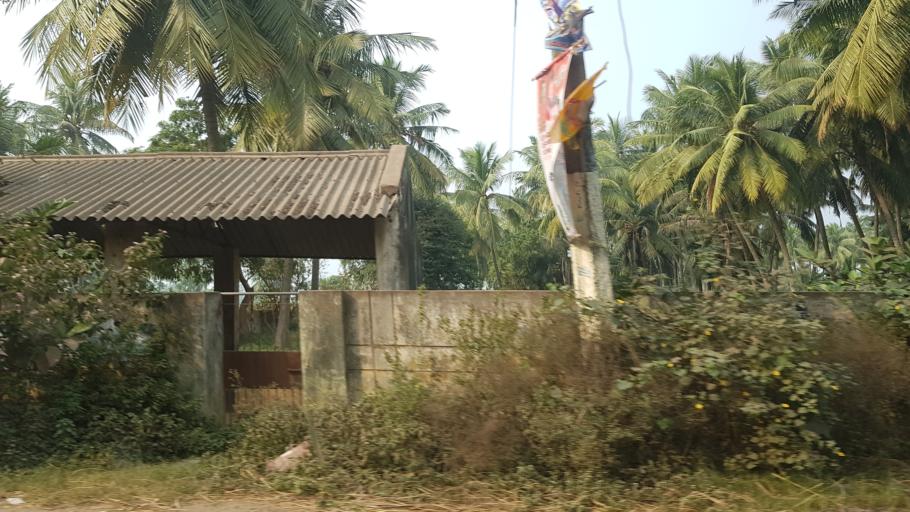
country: IN
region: Andhra Pradesh
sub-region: West Godavari
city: Akividu
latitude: 16.5376
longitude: 81.4160
